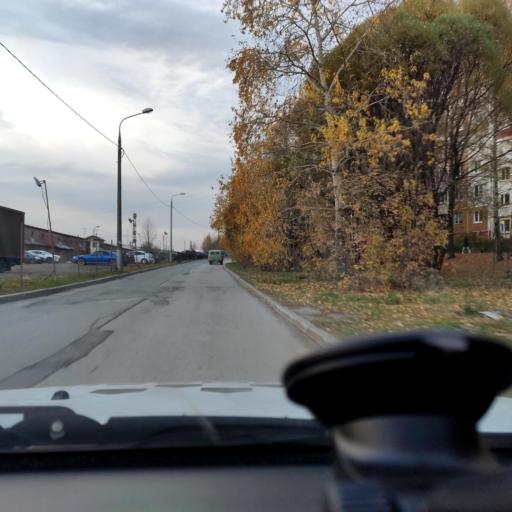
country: RU
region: Perm
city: Perm
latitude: 58.0078
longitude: 56.3136
